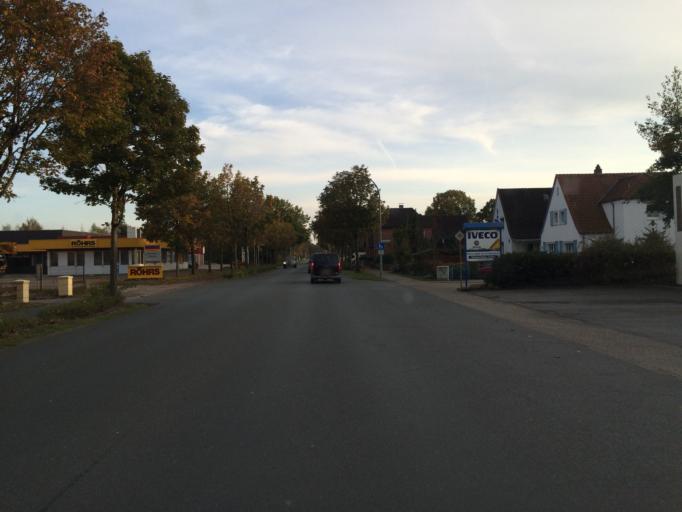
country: DE
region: Lower Saxony
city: Soltau
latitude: 52.9751
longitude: 9.8498
